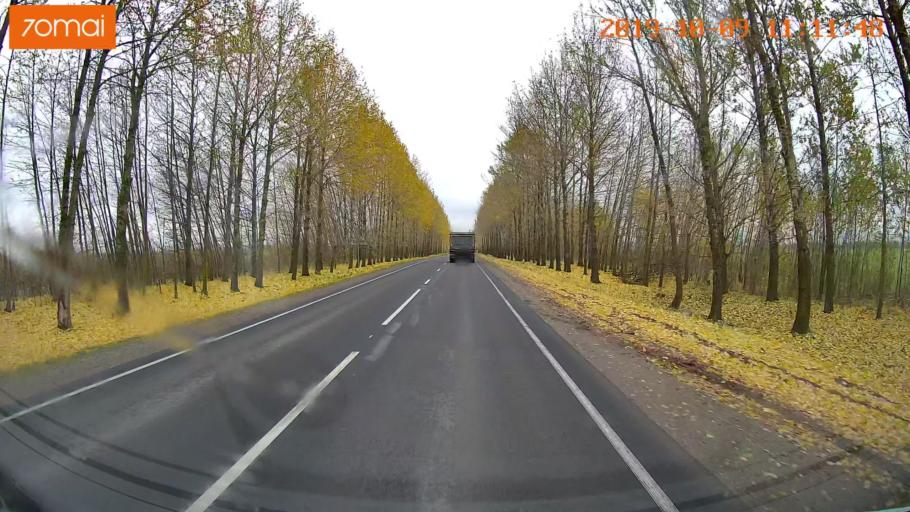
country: RU
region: Vologda
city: Vologda
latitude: 59.1716
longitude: 39.8239
